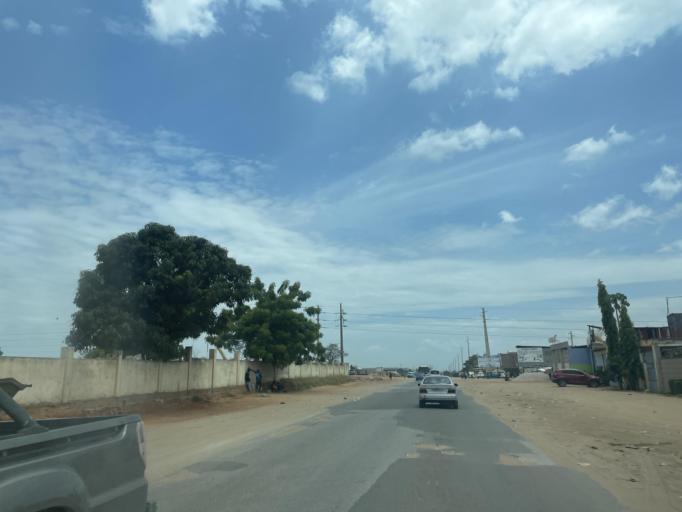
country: AO
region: Luanda
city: Luanda
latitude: -8.9359
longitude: 13.3822
